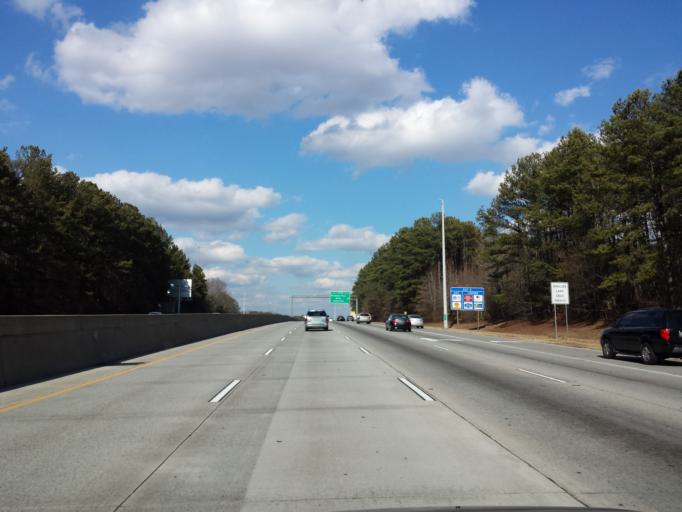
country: US
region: Georgia
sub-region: Fulton County
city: Alpharetta
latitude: 34.0811
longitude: -84.2655
